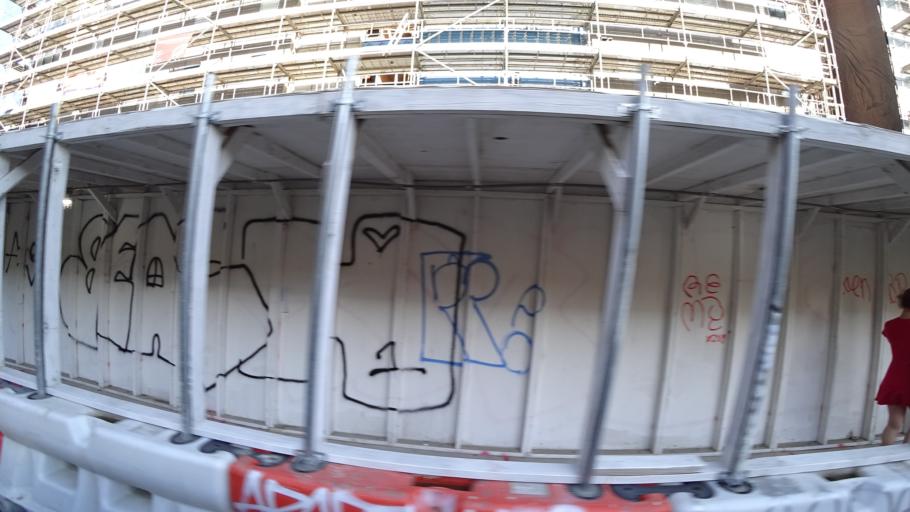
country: US
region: Texas
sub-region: Travis County
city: Austin
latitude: 30.2863
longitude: -97.7438
